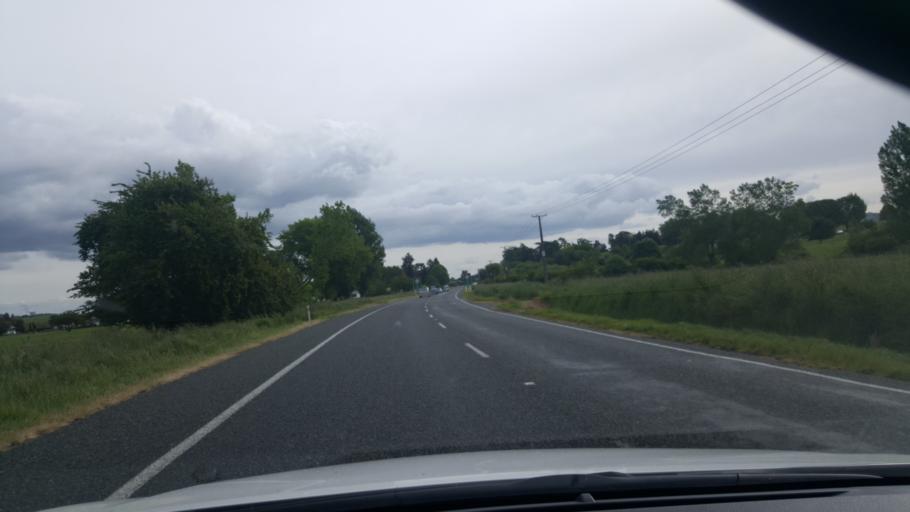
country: NZ
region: Waikato
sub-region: Taupo District
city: Taupo
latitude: -38.4652
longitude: 176.3133
